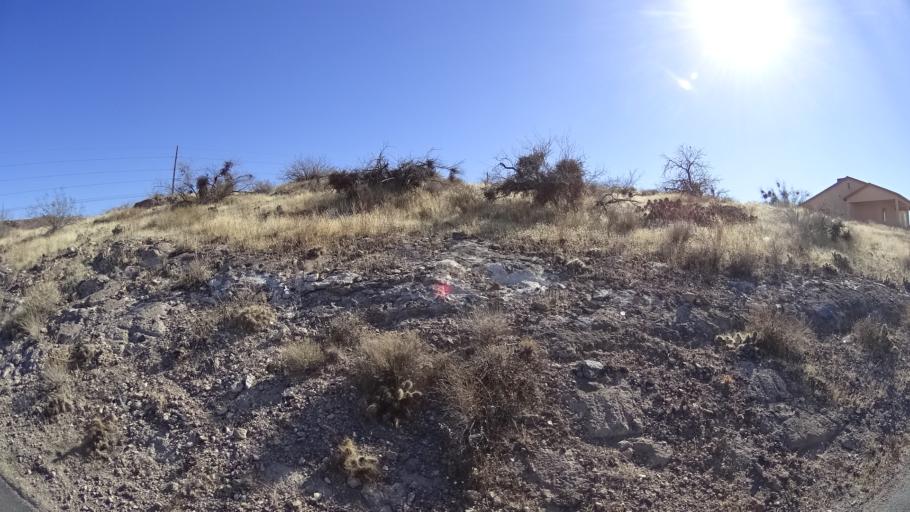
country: US
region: Arizona
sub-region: Mohave County
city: Kingman
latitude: 35.1846
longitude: -114.0492
